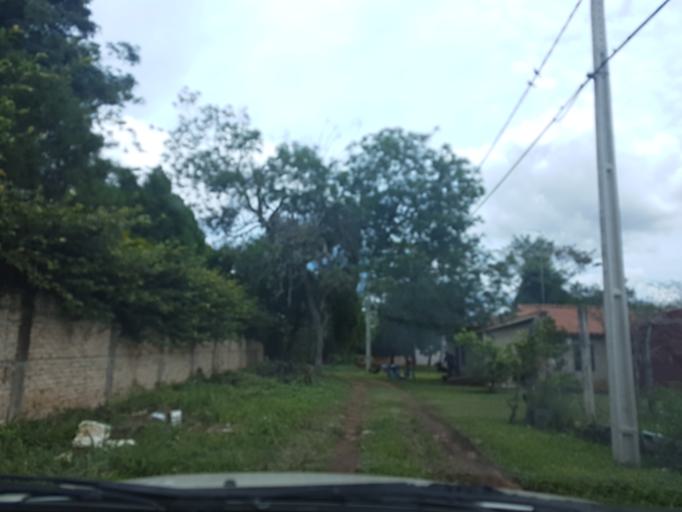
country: PY
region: Central
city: Colonia Mariano Roque Alonso
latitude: -25.1896
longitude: -57.5205
